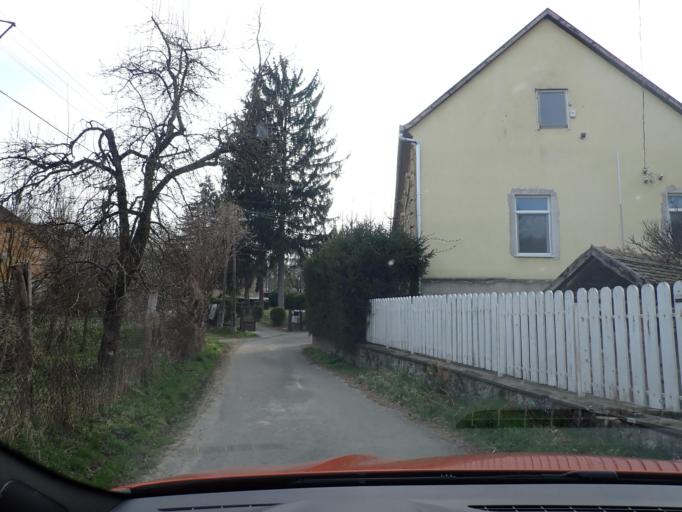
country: HU
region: Baranya
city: Komlo
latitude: 46.1613
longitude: 18.2428
